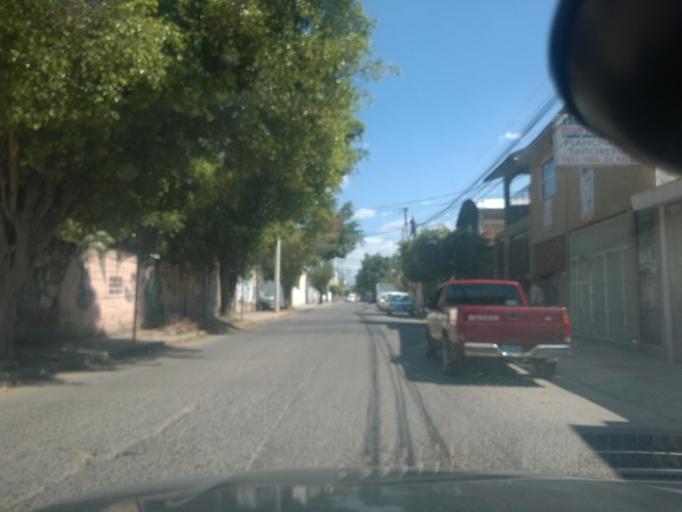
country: MX
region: Guanajuato
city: Leon
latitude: 21.1563
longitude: -101.6738
